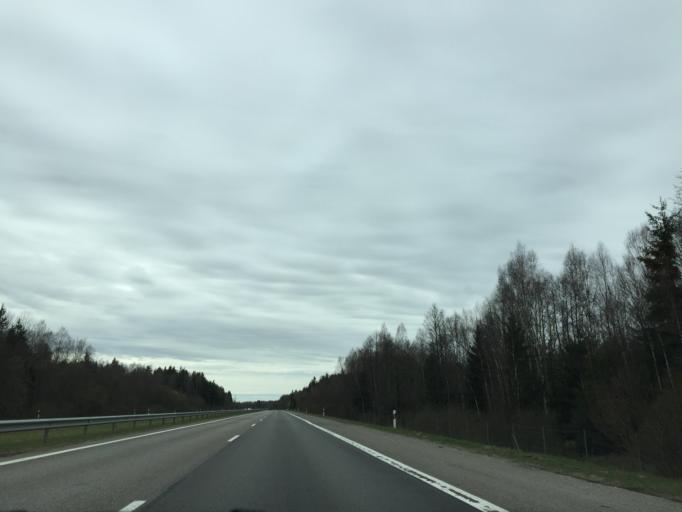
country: LT
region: Klaipedos apskritis
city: Gargzdai
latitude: 55.7020
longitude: 21.6144
